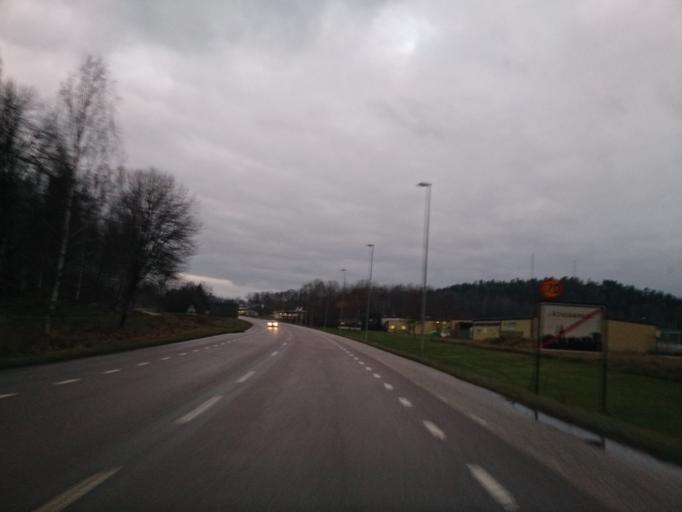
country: SE
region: OEstergoetland
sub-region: Atvidabergs Kommun
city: Atvidaberg
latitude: 58.2100
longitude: 15.9880
